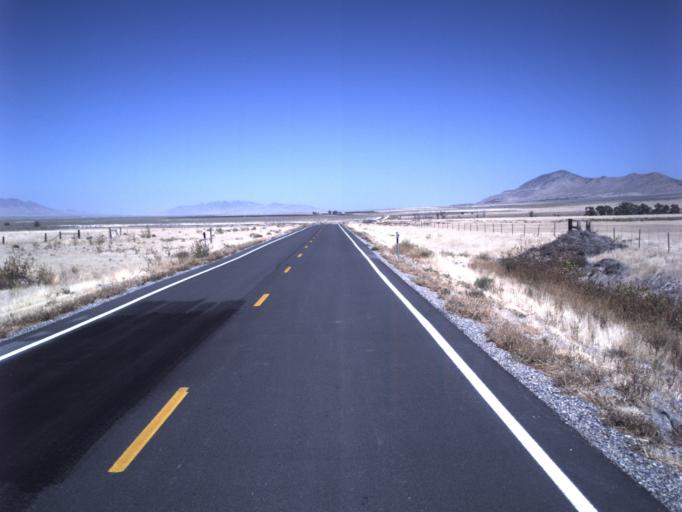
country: US
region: Utah
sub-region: Tooele County
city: Grantsville
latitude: 40.4436
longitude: -112.7486
